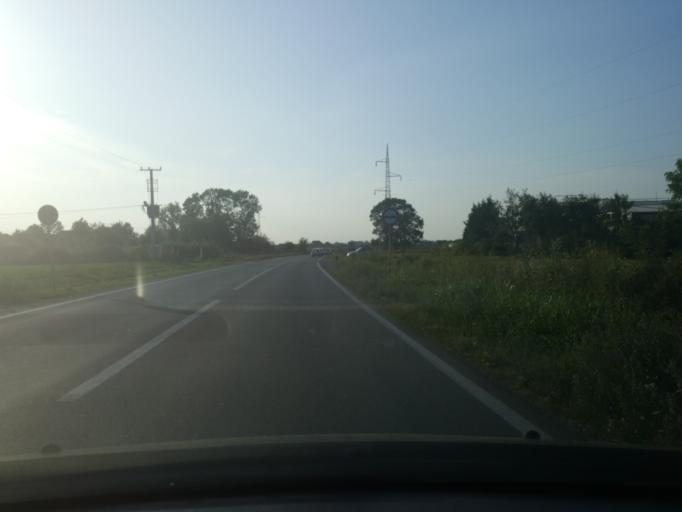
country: RS
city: Majur
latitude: 44.7670
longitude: 19.6306
